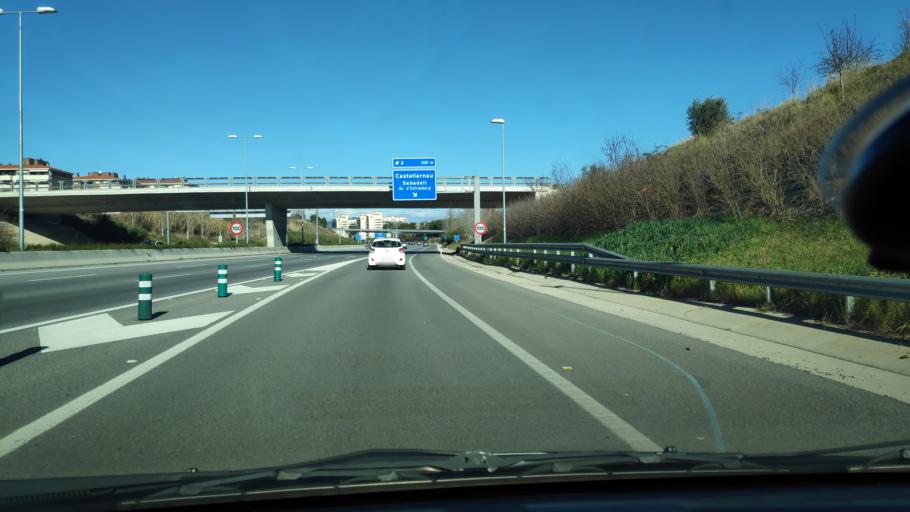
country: ES
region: Catalonia
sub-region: Provincia de Barcelona
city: Sant Quirze del Valles
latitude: 41.5529
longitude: 2.0770
